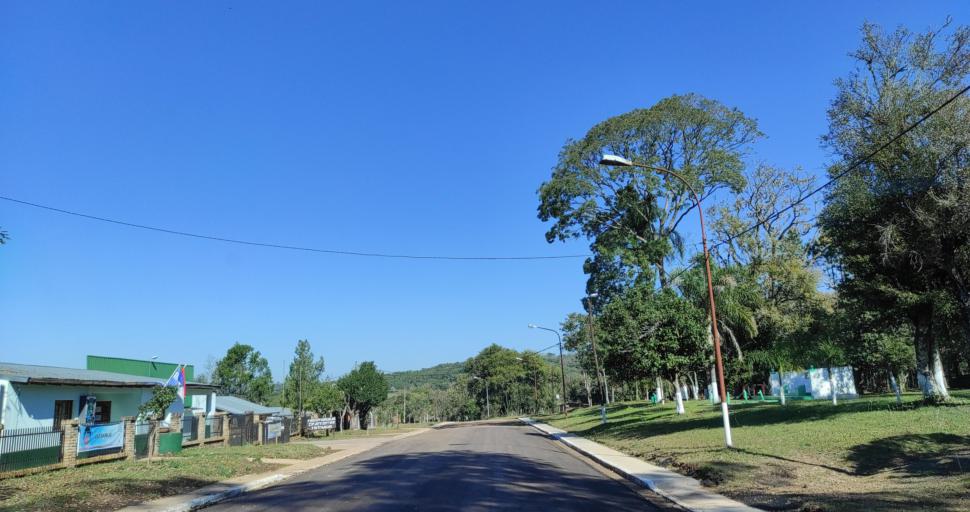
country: AR
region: Misiones
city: Cerro Cora
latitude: -27.6332
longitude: -55.7038
